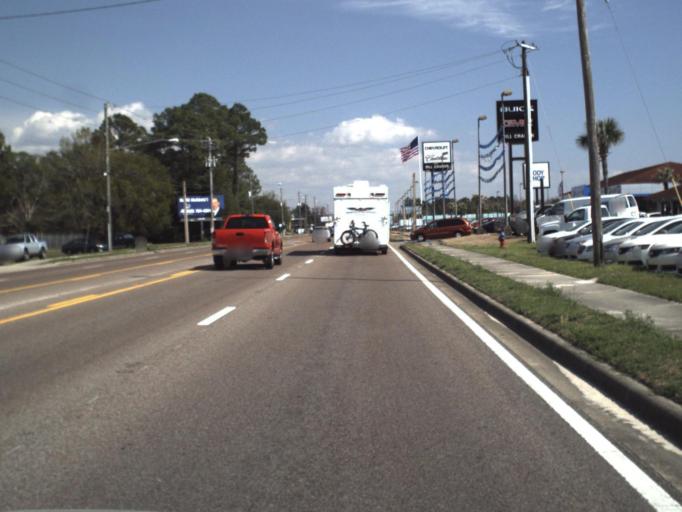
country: US
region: Florida
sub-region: Bay County
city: Pretty Bayou
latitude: 30.1897
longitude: -85.6954
